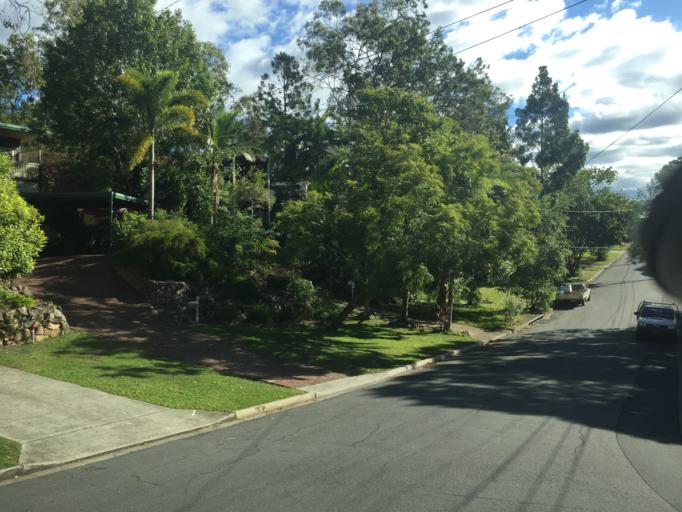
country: AU
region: Queensland
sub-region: Brisbane
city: Toowong
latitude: -27.4504
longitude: 152.9606
